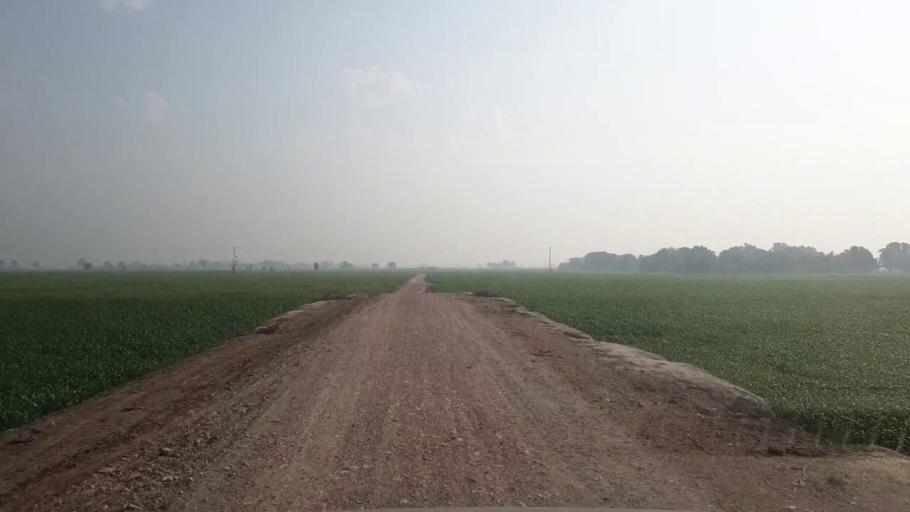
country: PK
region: Sindh
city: Hala
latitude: 25.8588
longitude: 68.4369
